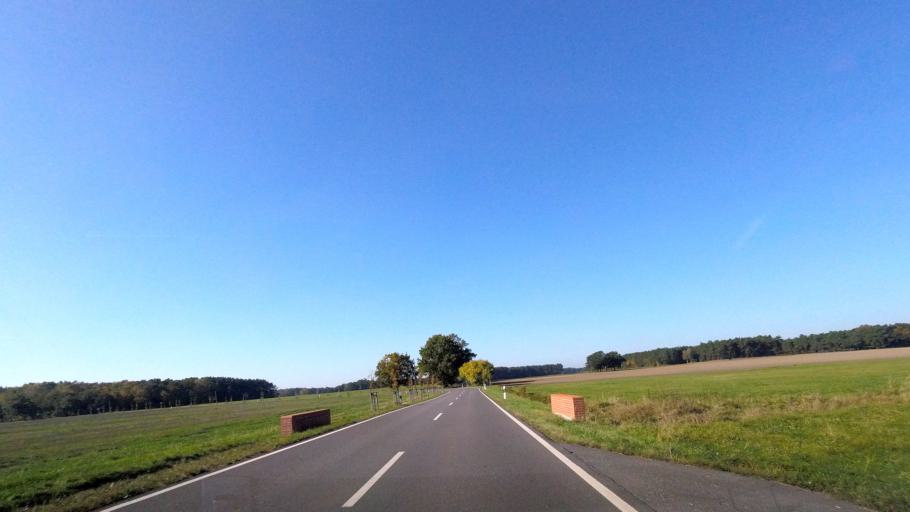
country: DE
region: Saxony-Anhalt
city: Zahna
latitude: 51.8840
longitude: 12.8130
